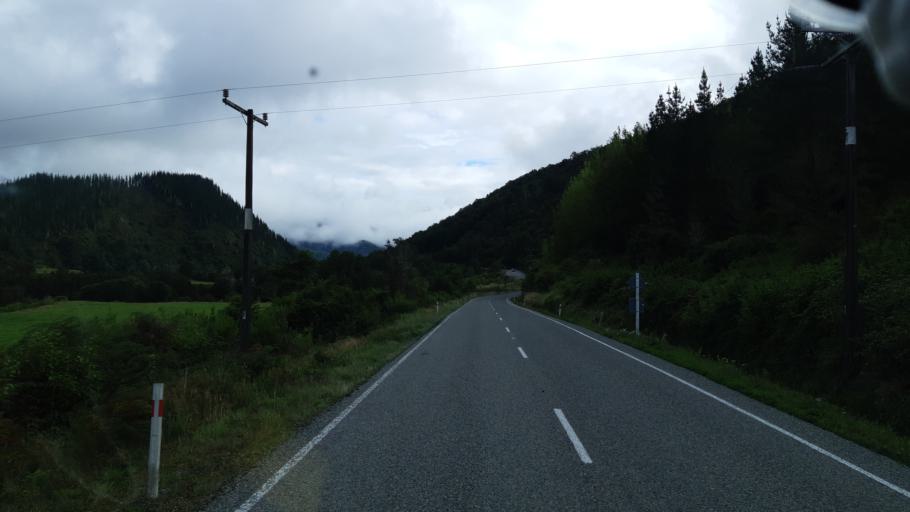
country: NZ
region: West Coast
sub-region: Buller District
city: Westport
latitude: -41.9699
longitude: 172.2040
